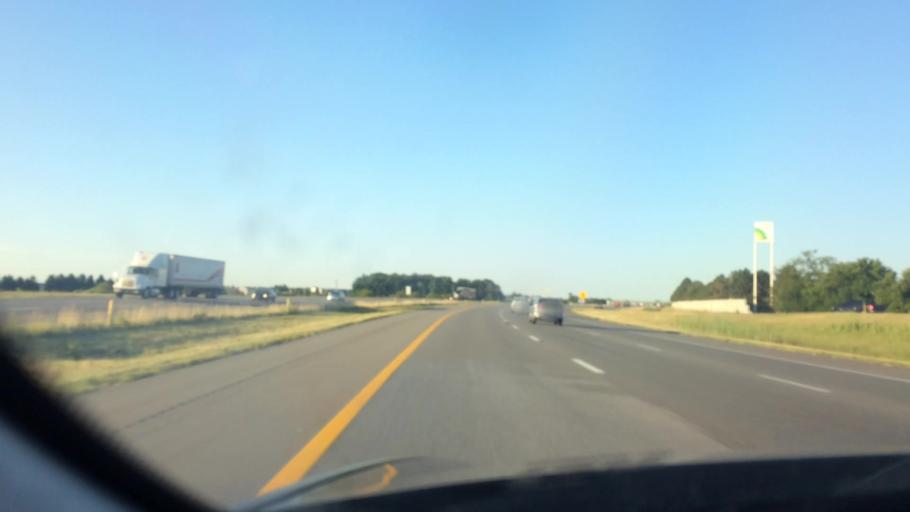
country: US
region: Ohio
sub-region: Wood County
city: Bowling Green
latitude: 41.3739
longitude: -83.6163
